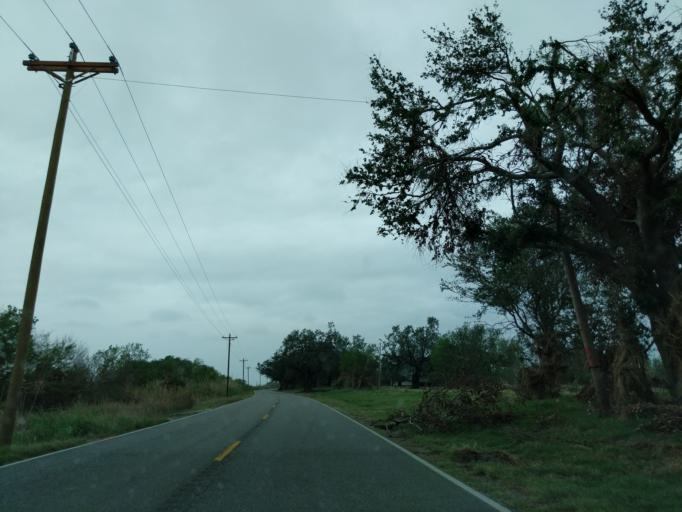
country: US
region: Louisiana
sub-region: Jefferson Davis Parish
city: Lake Arthur
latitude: 29.7523
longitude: -92.9098
